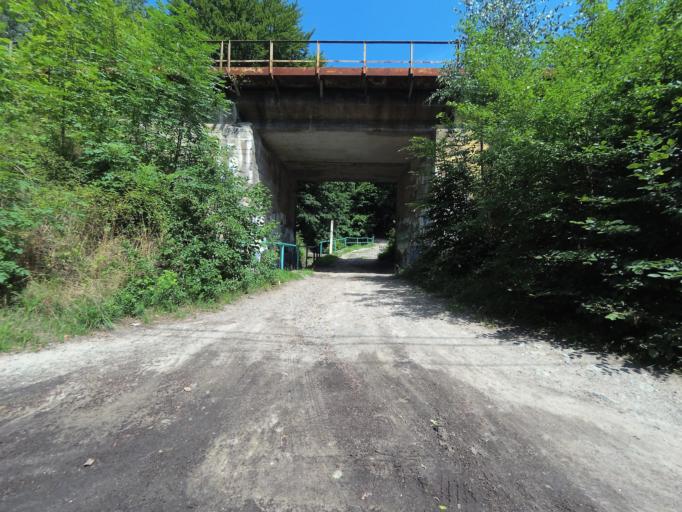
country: PL
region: Pomeranian Voivodeship
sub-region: Gdynia
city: Wielki Kack
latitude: 54.4866
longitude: 18.5079
